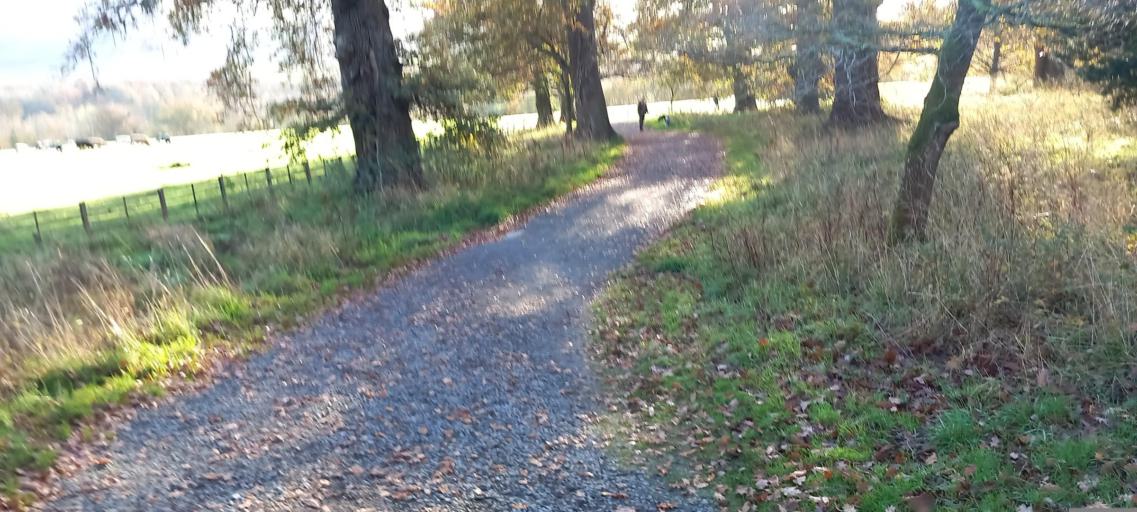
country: GB
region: Wales
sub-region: Anglesey
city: Beaumaris
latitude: 53.2269
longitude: -4.0935
